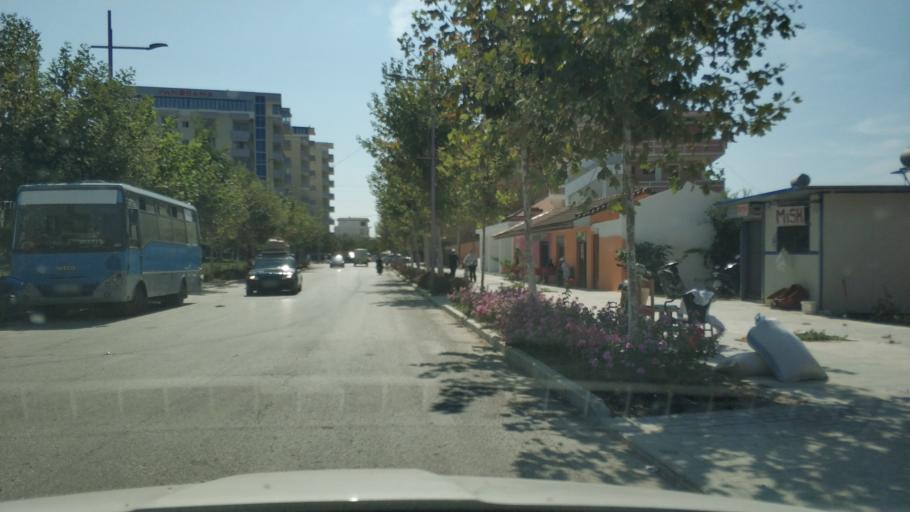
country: AL
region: Fier
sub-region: Rrethi i Lushnjes
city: Divjake
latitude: 40.9973
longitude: 19.5323
